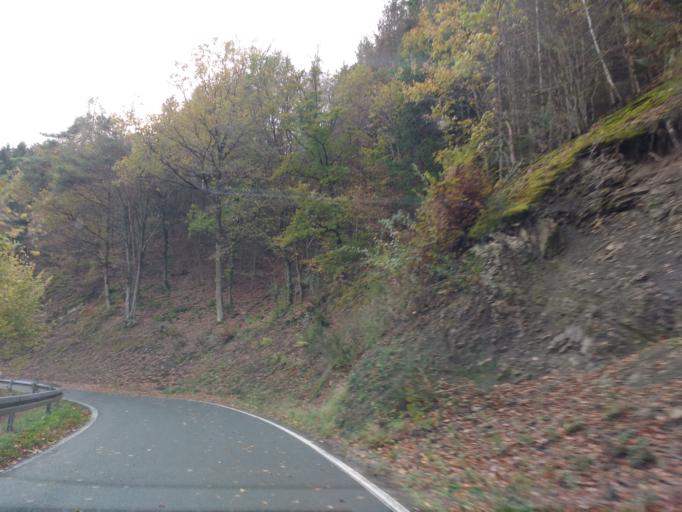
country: DE
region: Hesse
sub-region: Regierungsbezirk Kassel
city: Vohl
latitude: 51.1881
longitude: 8.9460
